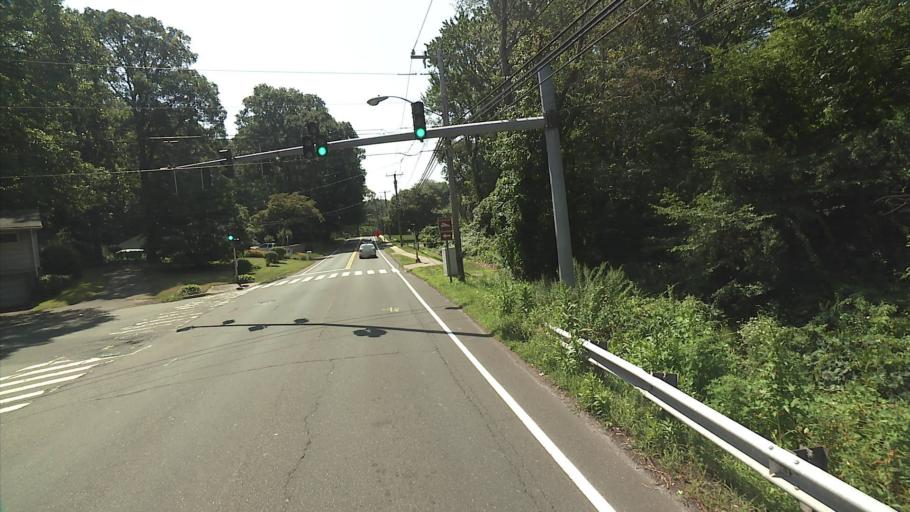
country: US
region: Connecticut
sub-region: New Haven County
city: Branford Center
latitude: 41.2680
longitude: -72.8315
